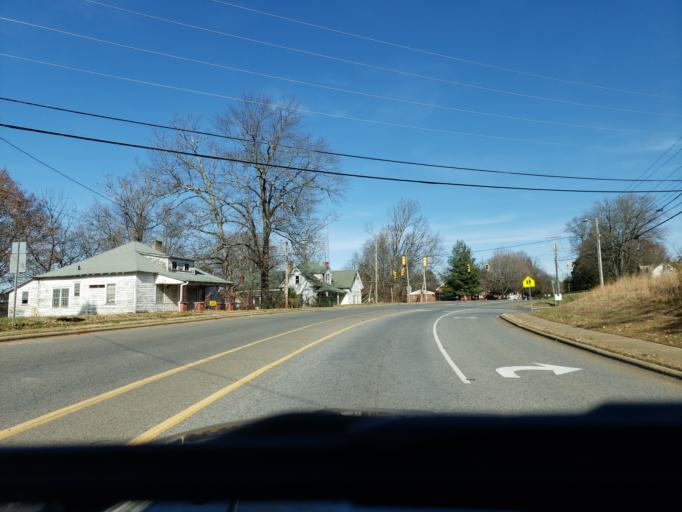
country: US
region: North Carolina
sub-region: Cleveland County
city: Kings Mountain
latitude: 35.2529
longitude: -81.3401
